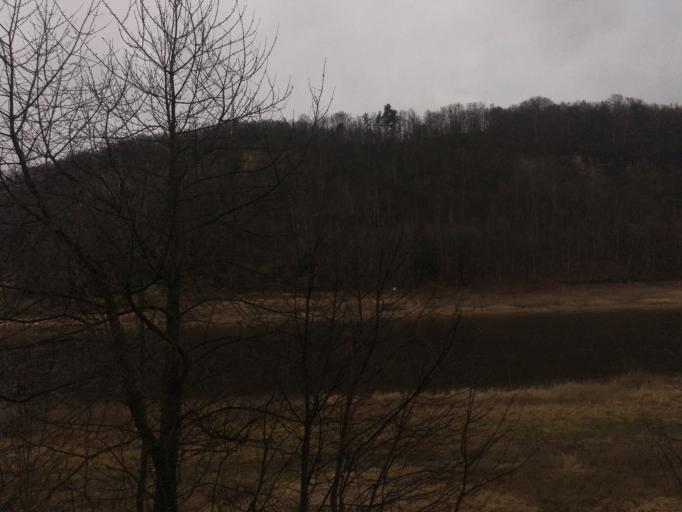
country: DE
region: Saxony
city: Struppen
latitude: 50.9453
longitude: 14.0128
